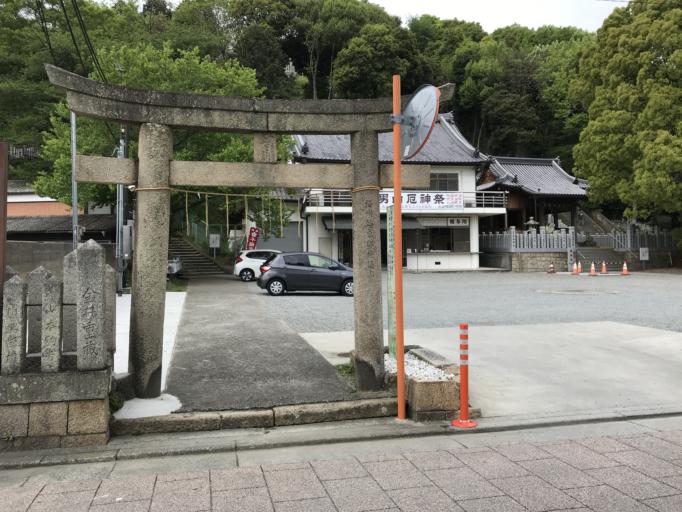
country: JP
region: Hyogo
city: Himeji
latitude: 34.8409
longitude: 134.6893
